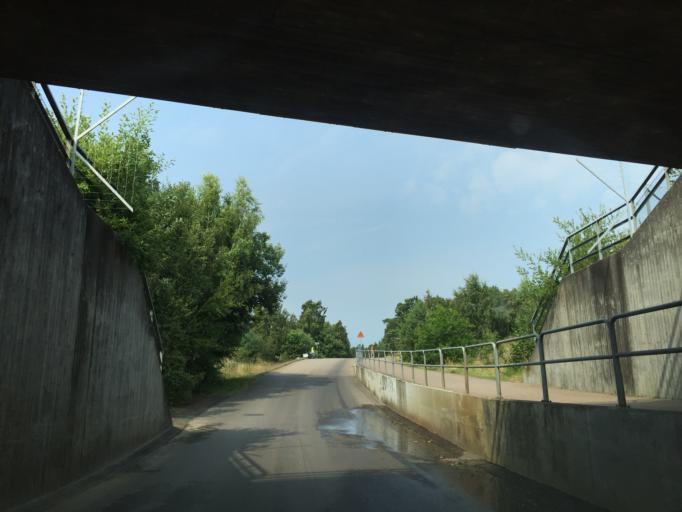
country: SE
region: Skane
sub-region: Angelholms Kommun
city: AEngelholm
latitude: 56.2308
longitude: 12.8327
